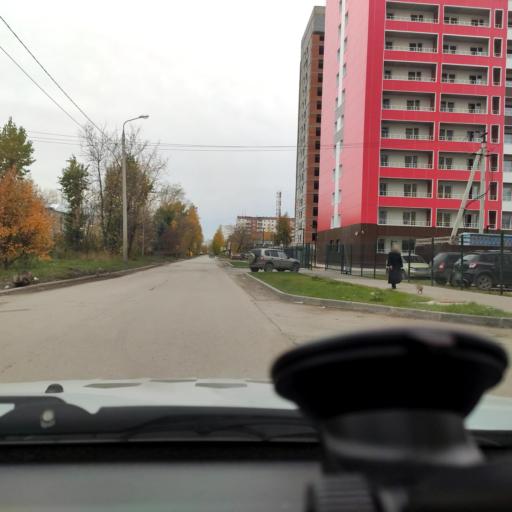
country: RU
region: Perm
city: Perm
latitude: 57.9684
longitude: 56.2355
